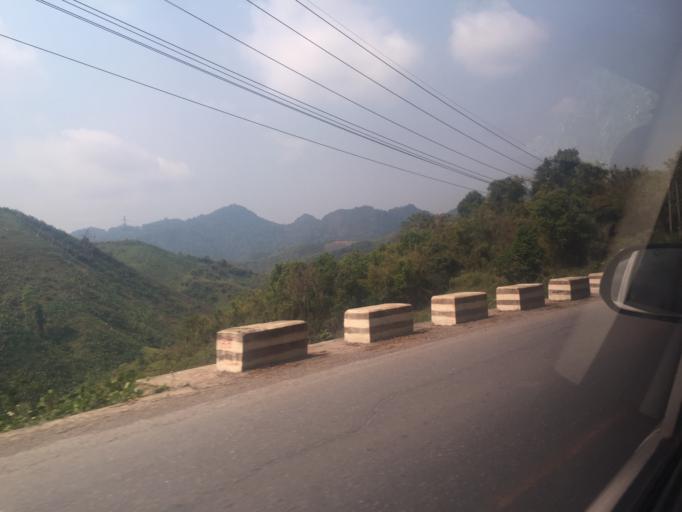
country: LA
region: Oudomxai
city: Muang Xay
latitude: 20.8537
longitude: 101.8121
